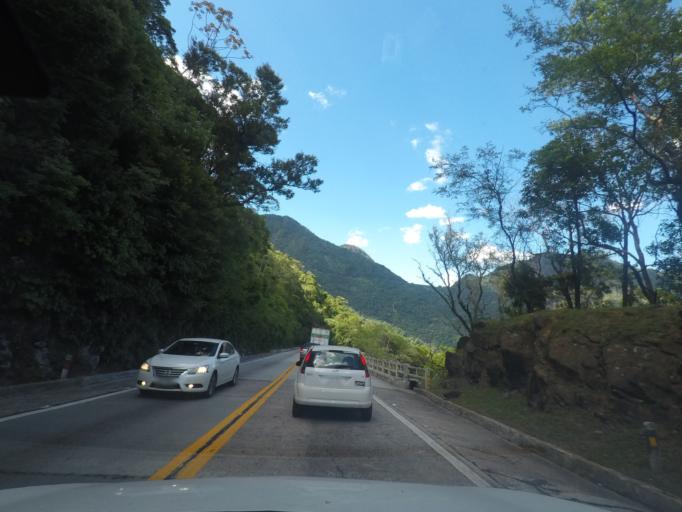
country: BR
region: Rio de Janeiro
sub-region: Guapimirim
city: Guapimirim
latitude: -22.4797
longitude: -42.9965
